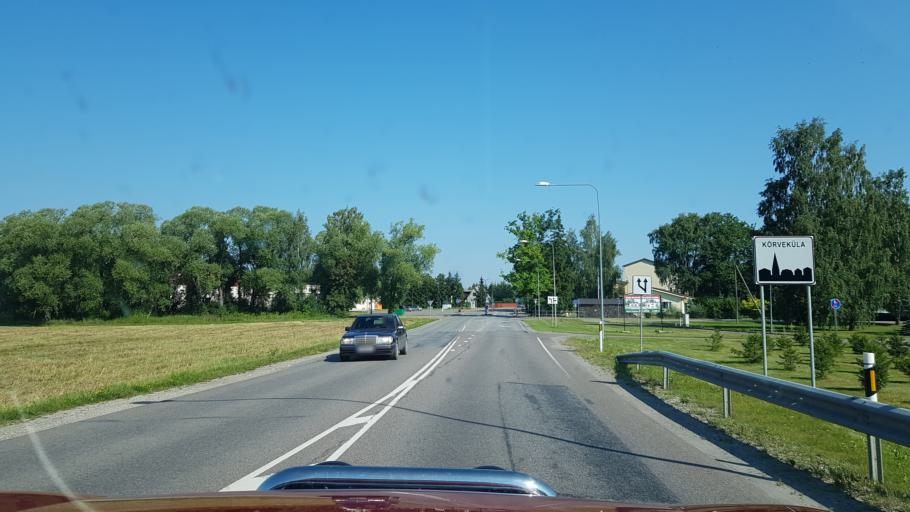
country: EE
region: Tartu
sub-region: Tartu linn
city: Tartu
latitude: 58.4179
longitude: 26.7634
